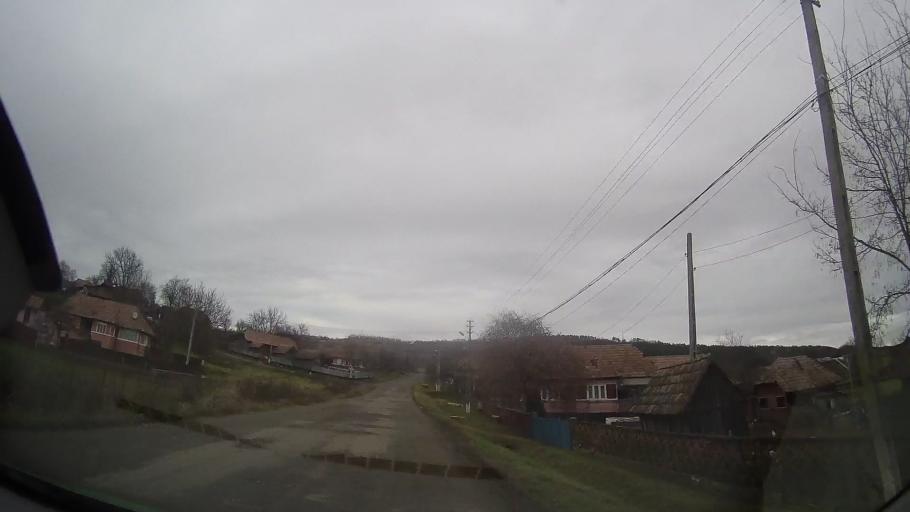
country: RO
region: Mures
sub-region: Comuna Bala
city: Bala
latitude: 46.7093
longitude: 24.5014
